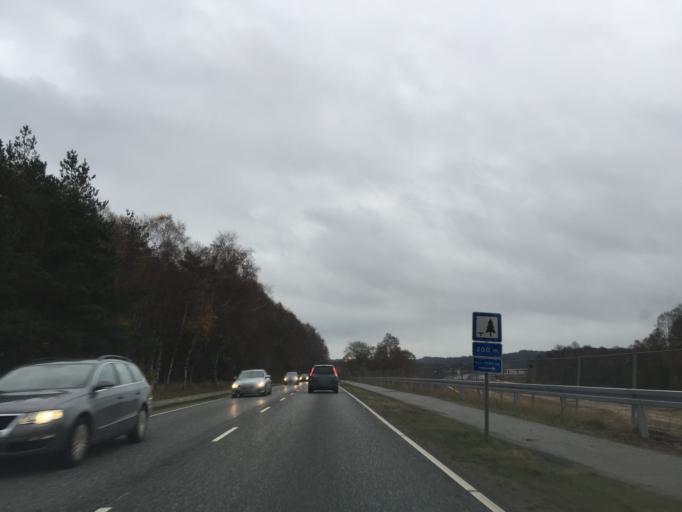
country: DK
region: Central Jutland
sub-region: Silkeborg Kommune
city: Silkeborg
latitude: 56.1783
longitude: 9.5935
